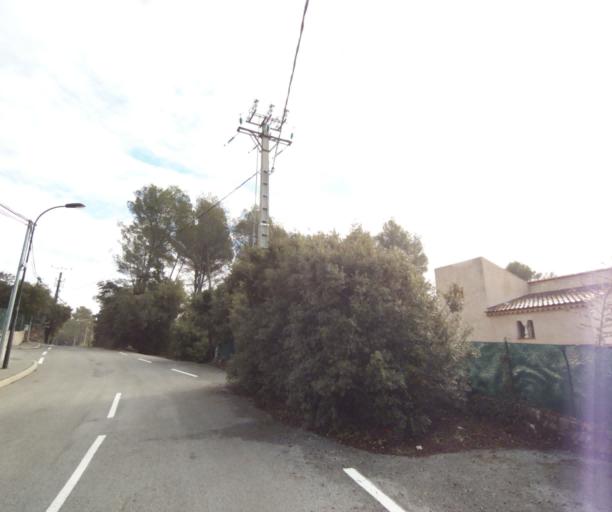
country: FR
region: Provence-Alpes-Cote d'Azur
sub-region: Departement du Var
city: Trans-en-Provence
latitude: 43.5023
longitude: 6.4952
